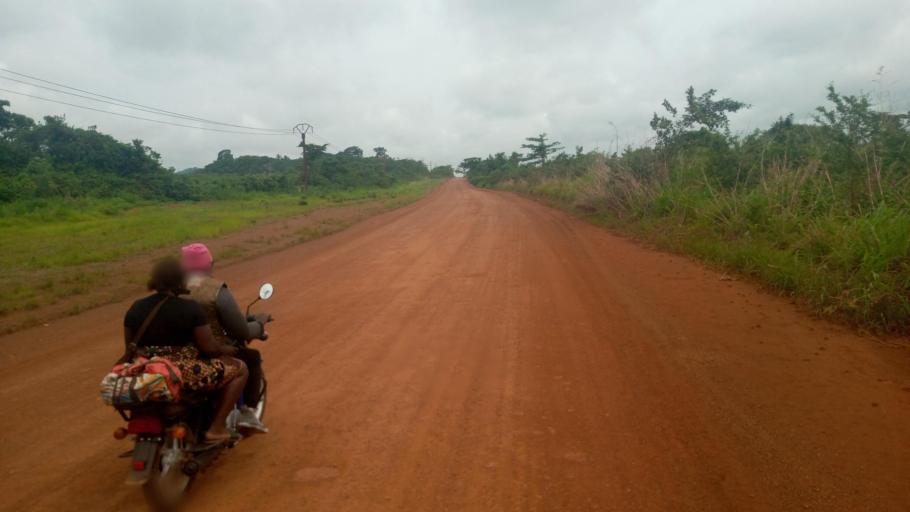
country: SL
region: Southern Province
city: Mogbwemo
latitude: 7.7380
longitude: -12.2810
